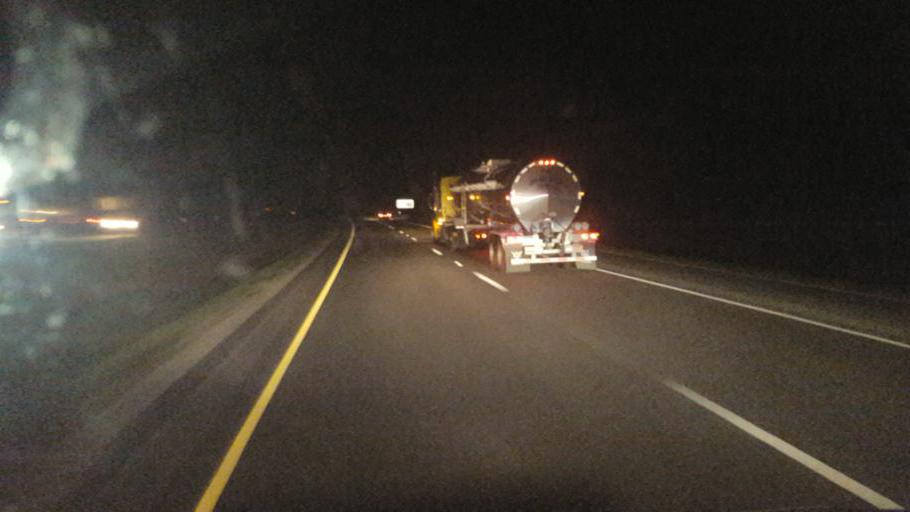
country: US
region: Ohio
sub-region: Preble County
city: New Paris
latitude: 39.8600
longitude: -84.8452
